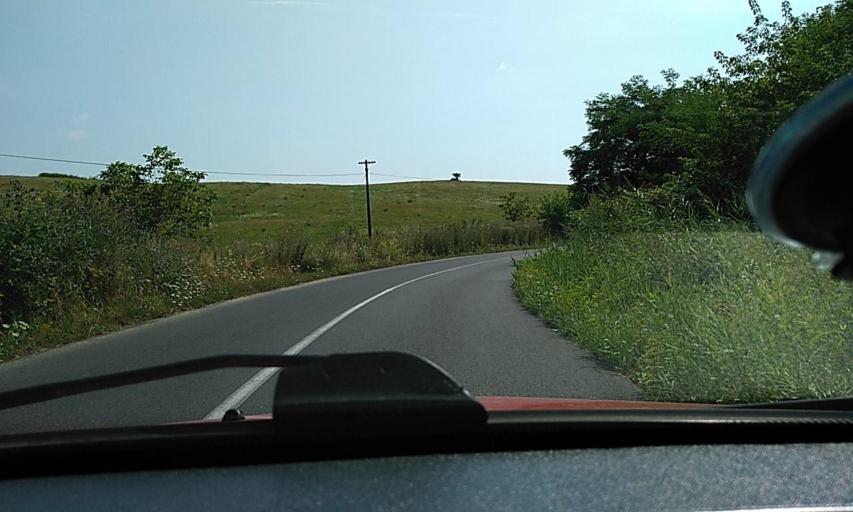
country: RO
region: Brasov
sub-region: Oras Rupea
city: Rupea
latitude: 46.0201
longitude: 25.1869
